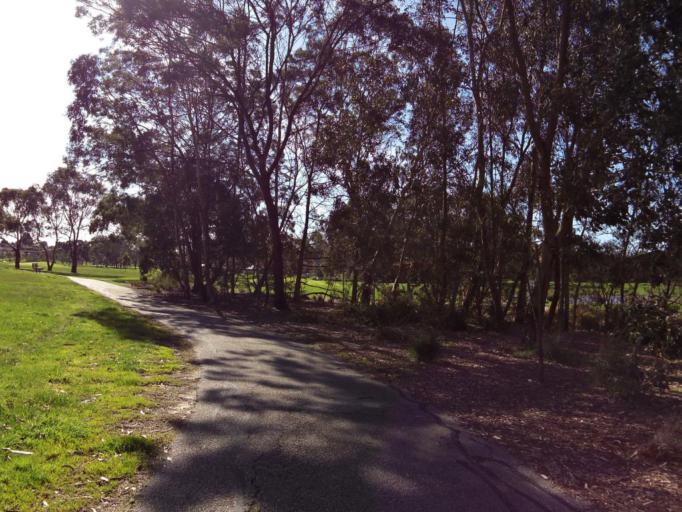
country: AU
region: Victoria
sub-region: Knox
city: Rowville
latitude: -37.9476
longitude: 145.2229
